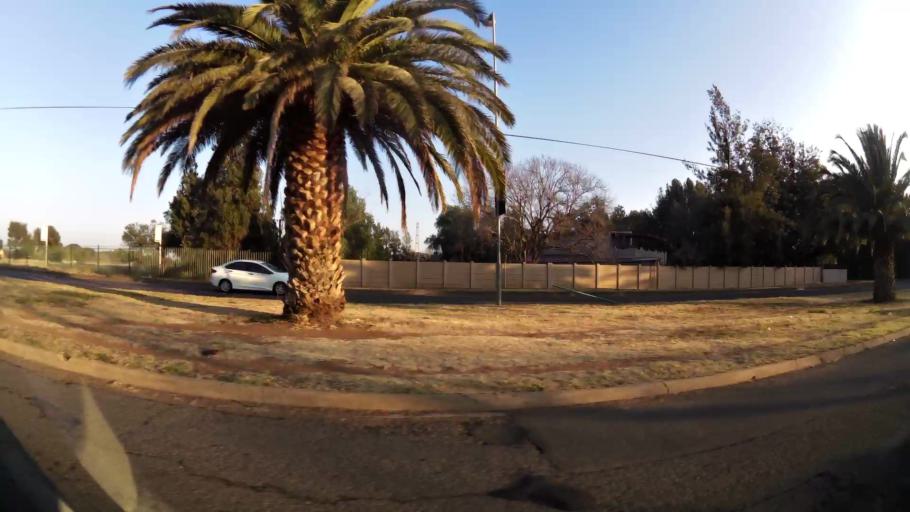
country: ZA
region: Orange Free State
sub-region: Mangaung Metropolitan Municipality
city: Bloemfontein
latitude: -29.0863
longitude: 26.1552
